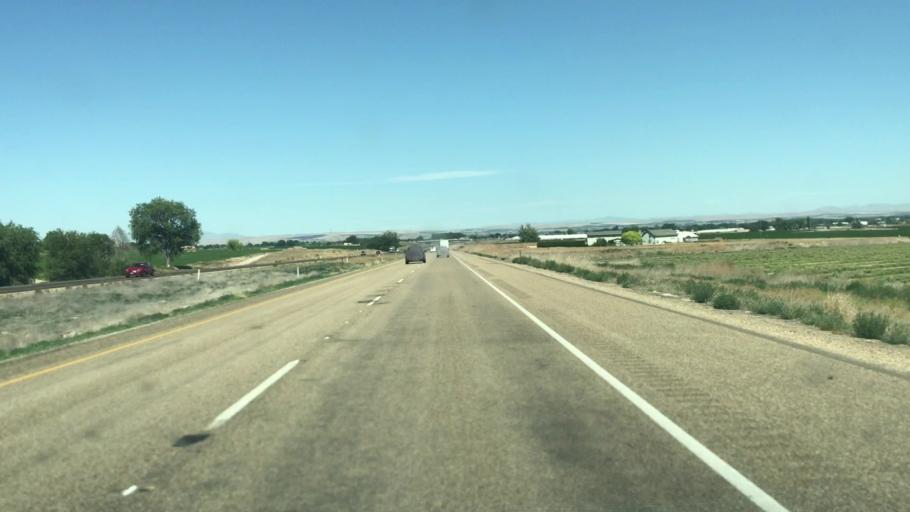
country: US
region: Idaho
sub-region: Payette County
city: New Plymouth
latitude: 43.9488
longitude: -116.8813
